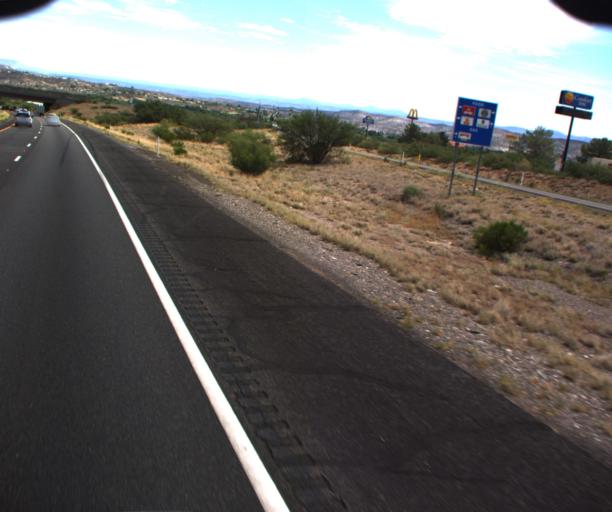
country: US
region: Arizona
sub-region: Yavapai County
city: Camp Verde
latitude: 34.5753
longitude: -111.8857
